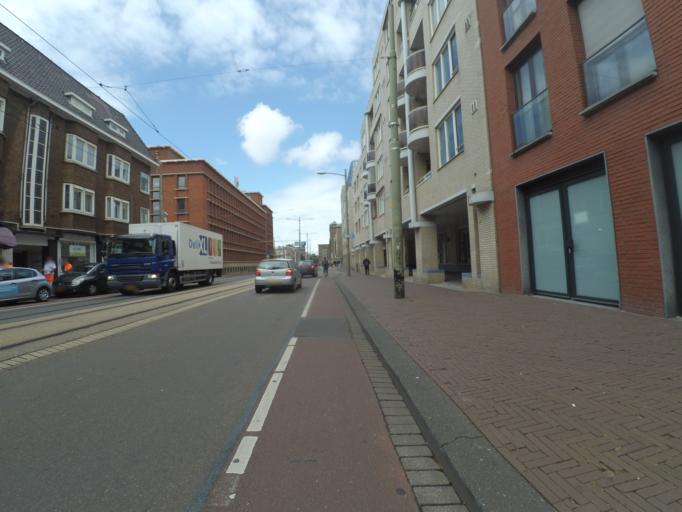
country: NL
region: South Holland
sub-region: Gemeente Den Haag
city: The Hague
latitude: 52.0789
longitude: 4.3038
